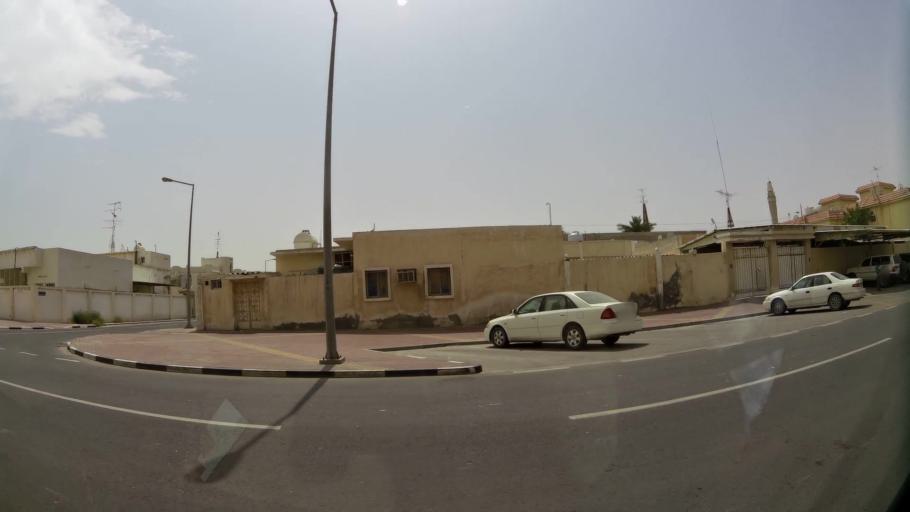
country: QA
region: Baladiyat ar Rayyan
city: Ar Rayyan
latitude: 25.3151
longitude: 51.4730
